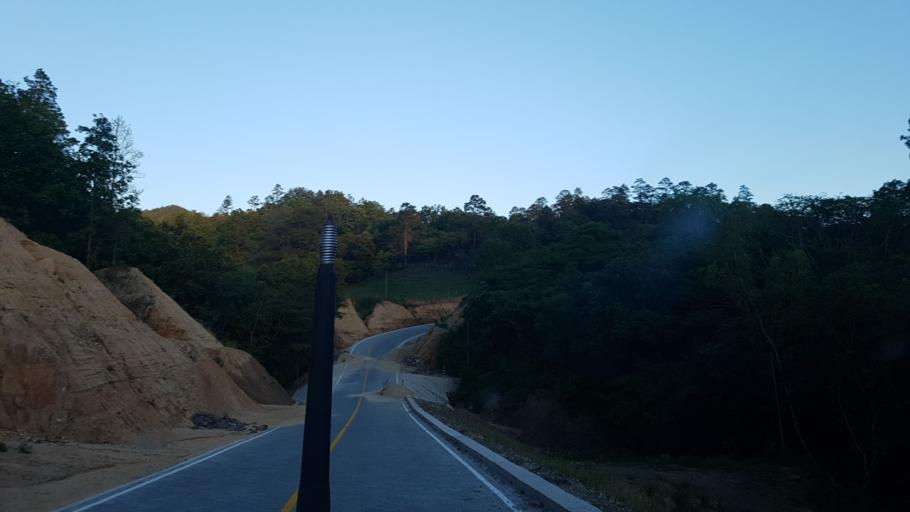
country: NI
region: Nueva Segovia
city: Ocotal
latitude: 13.6808
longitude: -86.6222
